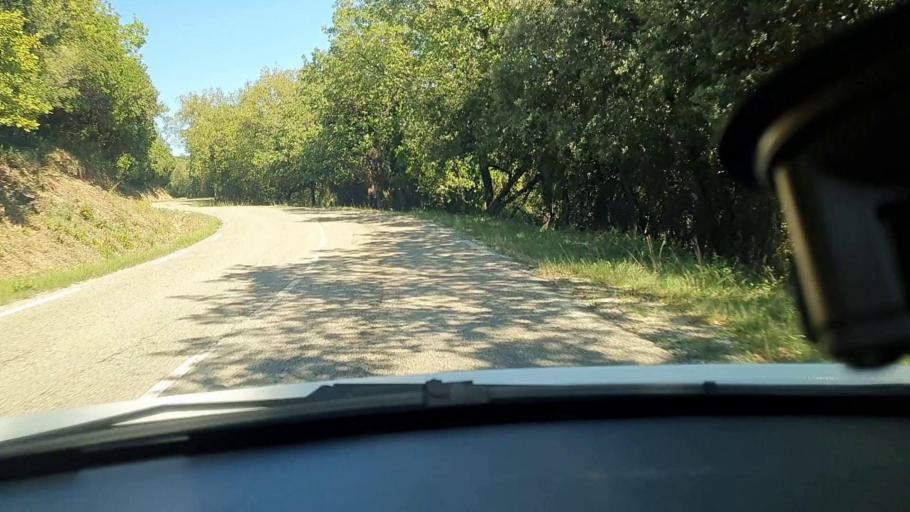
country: FR
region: Languedoc-Roussillon
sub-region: Departement du Gard
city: Saint-Paulet-de-Caisson
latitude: 44.2379
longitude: 4.5652
